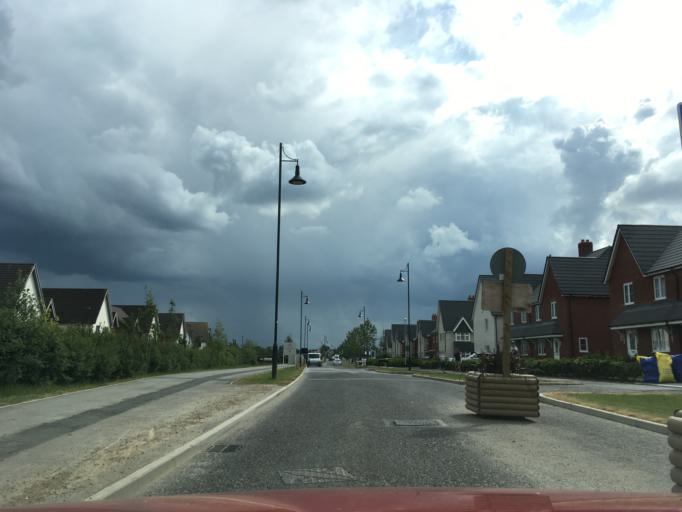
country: GB
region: England
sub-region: Wiltshire
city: Cricklade
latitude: 51.6096
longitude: -1.8254
